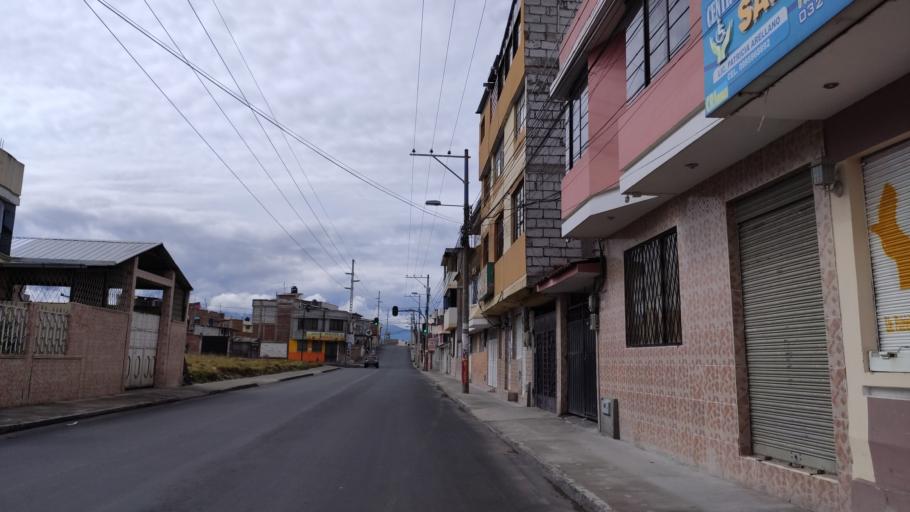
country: EC
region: Chimborazo
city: Riobamba
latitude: -1.6572
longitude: -78.6439
